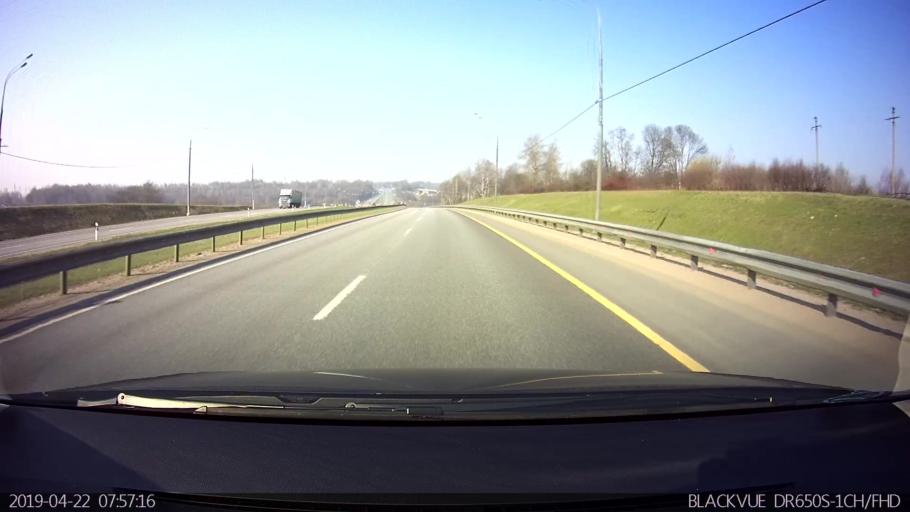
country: RU
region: Smolensk
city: Safonovo
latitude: 55.1369
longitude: 33.2141
